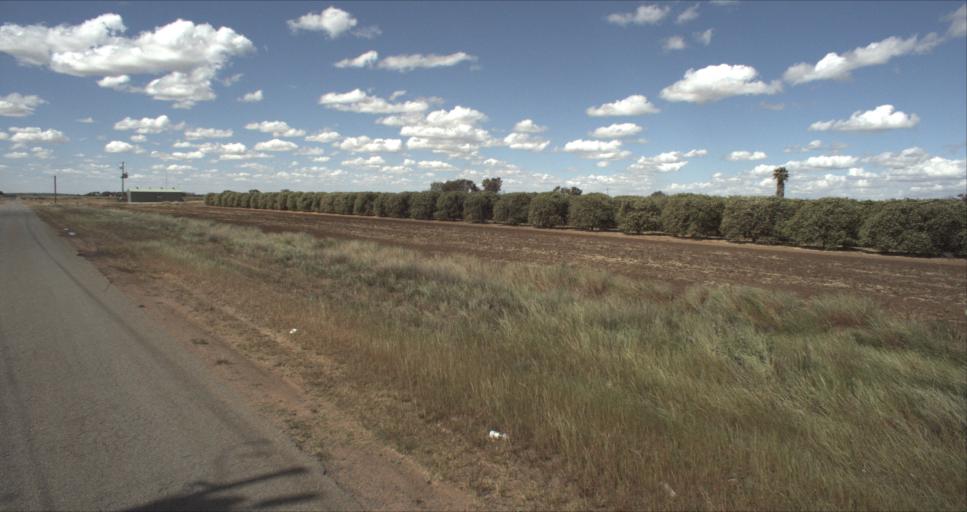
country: AU
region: New South Wales
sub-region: Leeton
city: Leeton
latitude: -34.5100
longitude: 146.2538
